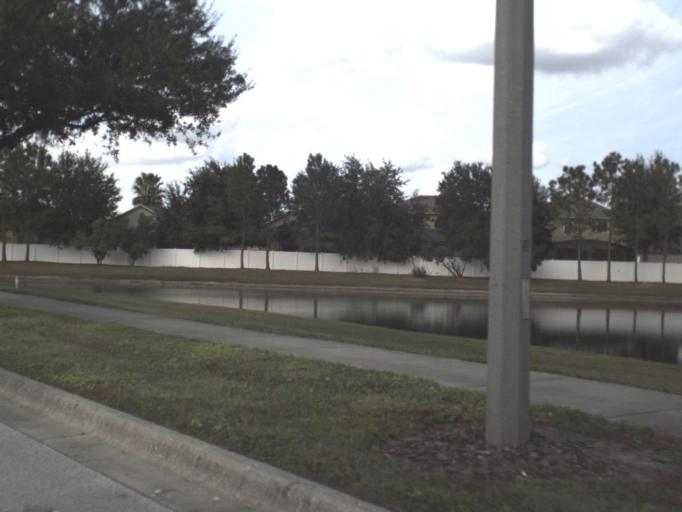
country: US
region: Florida
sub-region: Orange County
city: Conway
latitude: 28.4197
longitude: -81.2447
